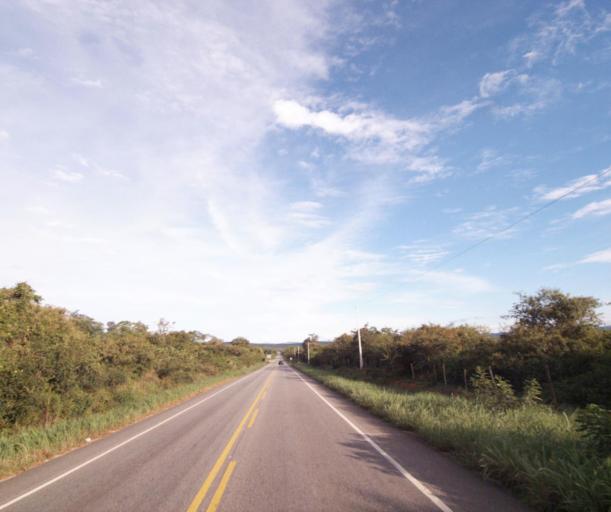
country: BR
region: Bahia
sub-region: Caetite
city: Caetite
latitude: -14.1207
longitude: -42.4259
